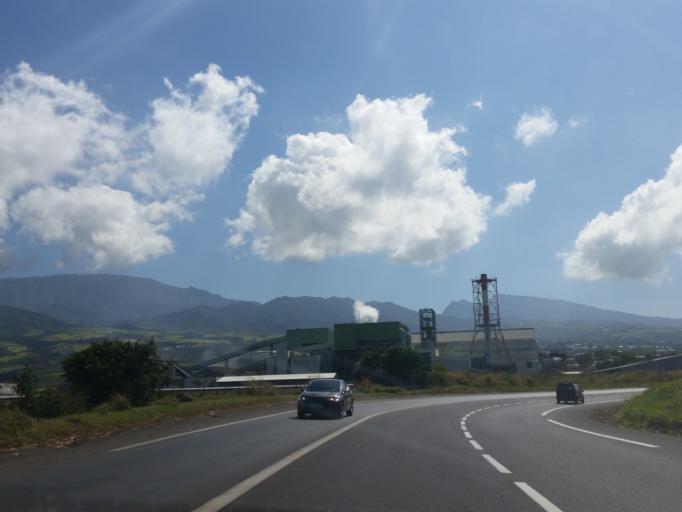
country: RE
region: Reunion
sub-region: Reunion
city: Saint-Louis
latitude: -21.2835
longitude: 55.3956
